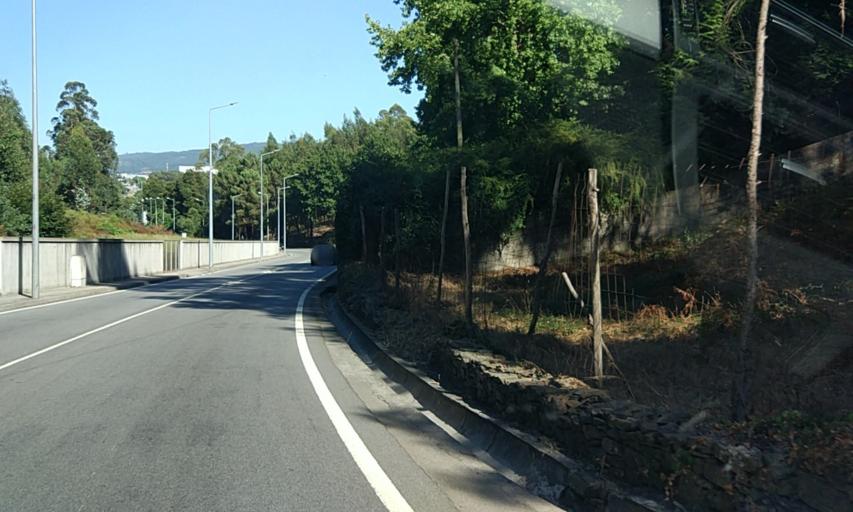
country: PT
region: Braga
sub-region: Vila Nova de Famalicao
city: Ferreiros
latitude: 41.3397
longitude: -8.5214
